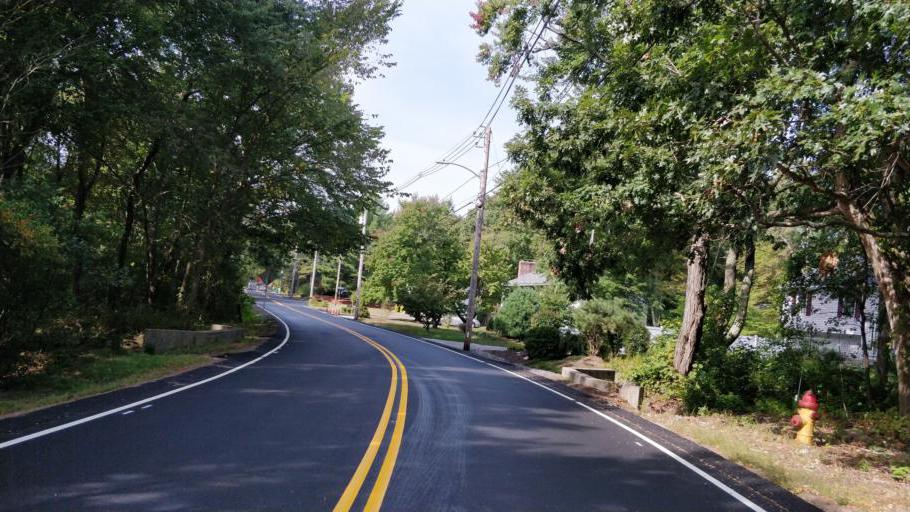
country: US
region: Massachusetts
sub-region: Bristol County
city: North Seekonk
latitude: 41.9048
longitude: -71.3231
